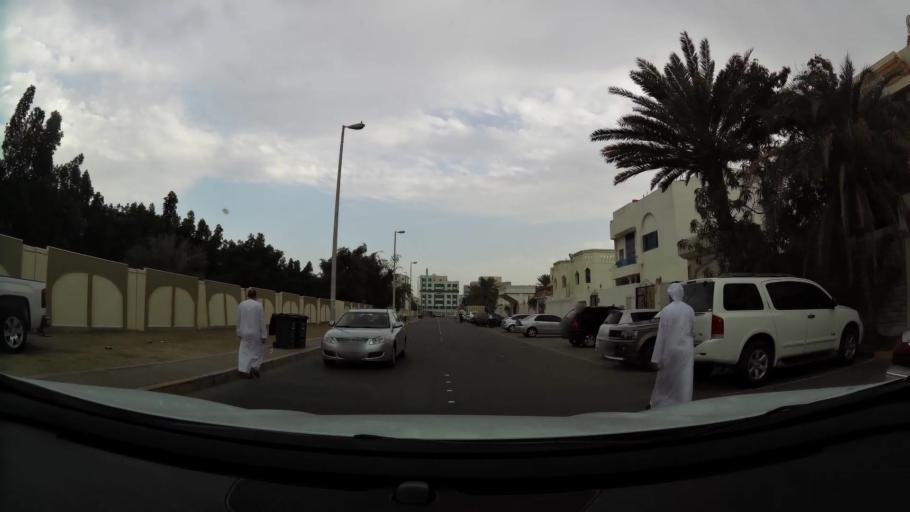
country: AE
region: Abu Dhabi
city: Abu Dhabi
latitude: 24.4772
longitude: 54.3750
